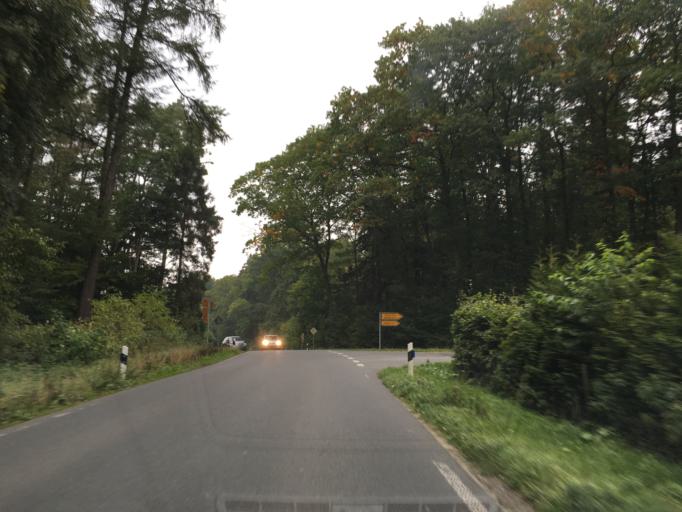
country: DE
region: Schleswig-Holstein
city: Salem
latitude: 53.6582
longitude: 10.8056
